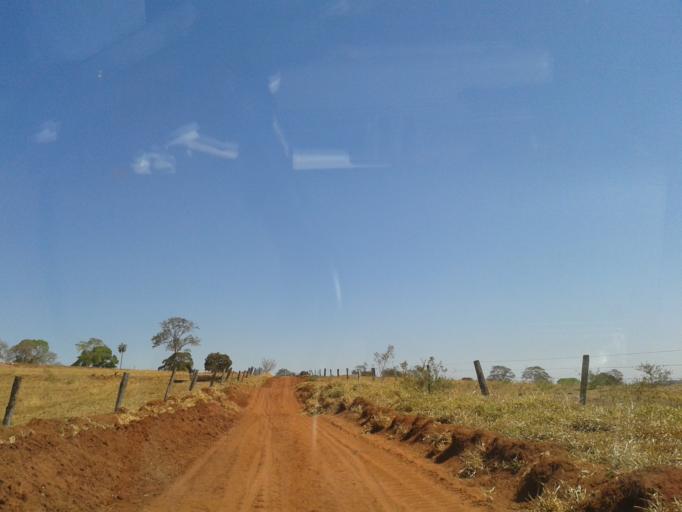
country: BR
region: Minas Gerais
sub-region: Santa Vitoria
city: Santa Vitoria
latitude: -19.0725
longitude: -50.0577
